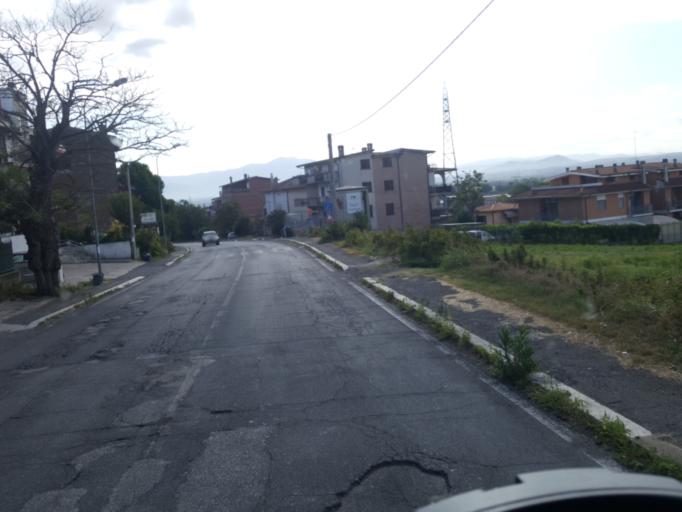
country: IT
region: Latium
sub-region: Citta metropolitana di Roma Capitale
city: Bivio di Capanelle
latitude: 42.1233
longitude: 12.5846
